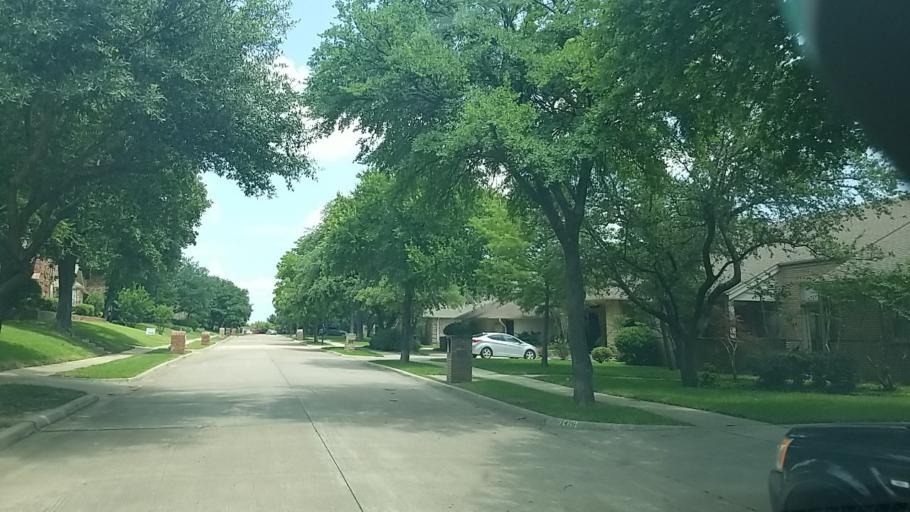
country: US
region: Texas
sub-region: Denton County
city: Corinth
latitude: 33.1608
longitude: -97.0866
